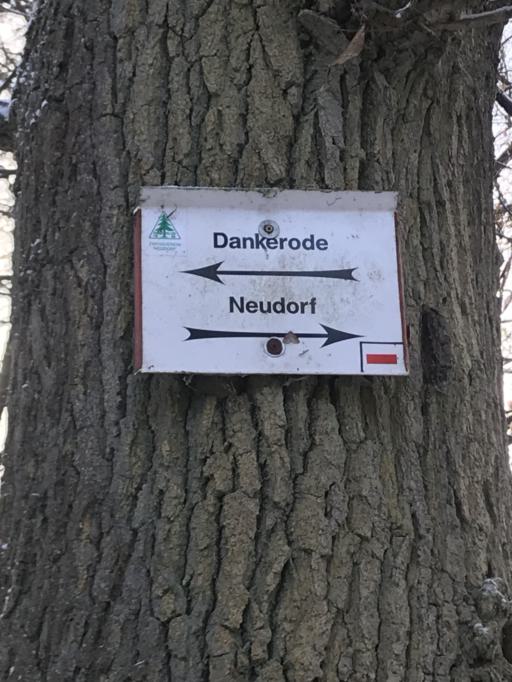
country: DE
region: Saxony-Anhalt
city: Harzgerode
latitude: 51.6009
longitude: 11.1284
